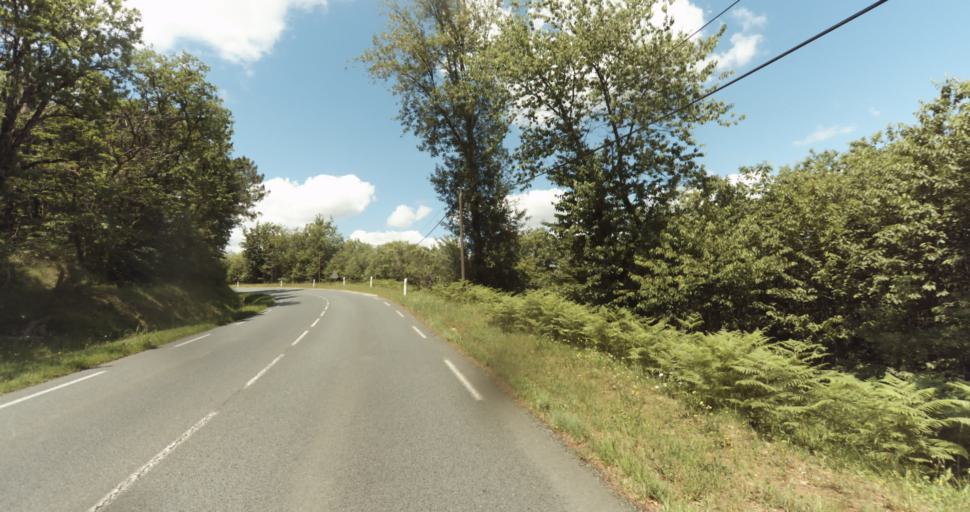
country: FR
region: Aquitaine
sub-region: Departement de la Dordogne
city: Le Bugue
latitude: 44.8421
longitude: 0.8762
